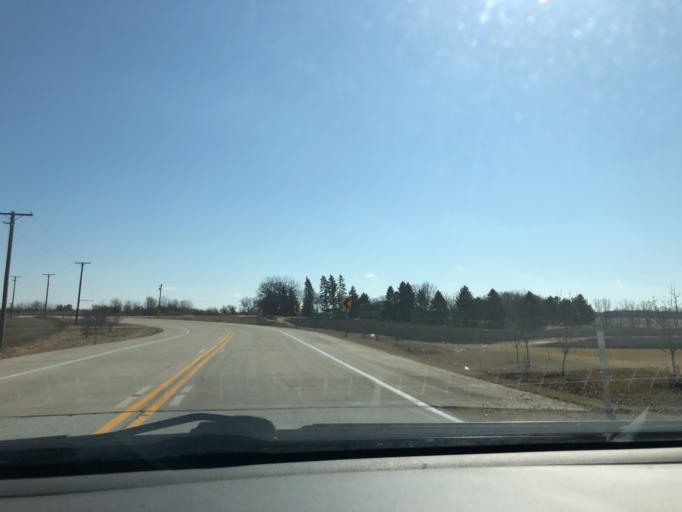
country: US
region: Illinois
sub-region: Kane County
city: Hampshire
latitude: 42.1028
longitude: -88.4853
